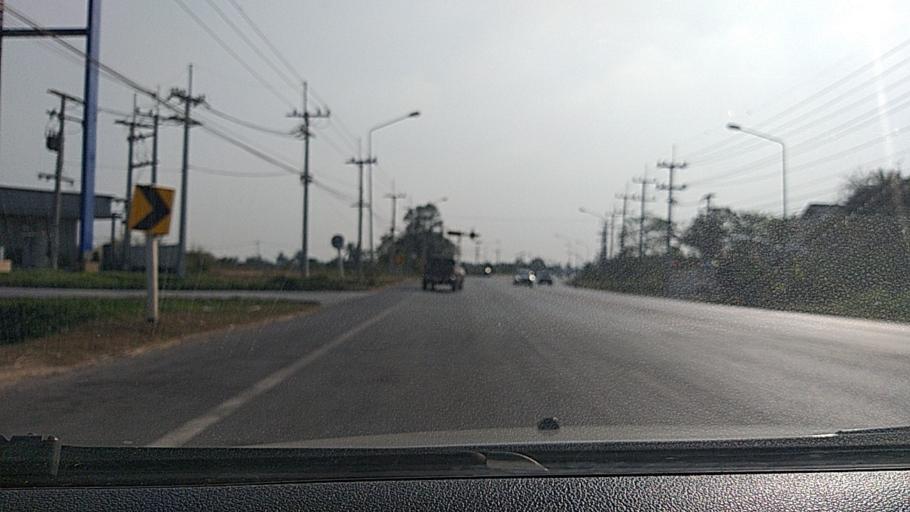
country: TH
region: Sing Buri
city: Sing Buri
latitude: 14.8616
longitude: 100.3950
